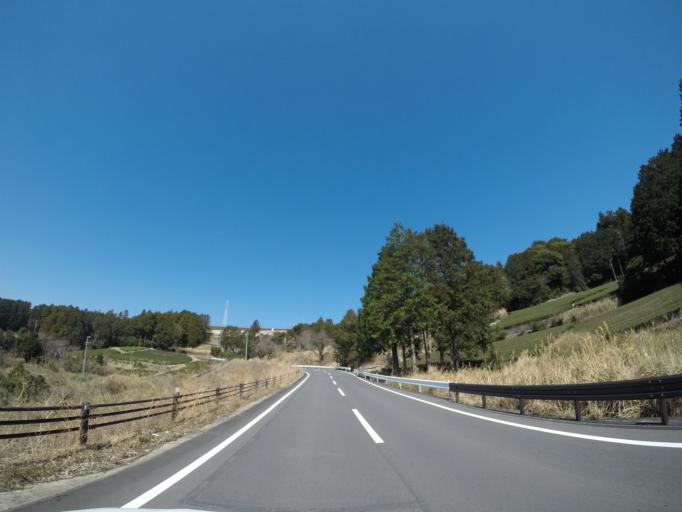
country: JP
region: Shizuoka
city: Kanaya
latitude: 34.8089
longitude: 138.1239
